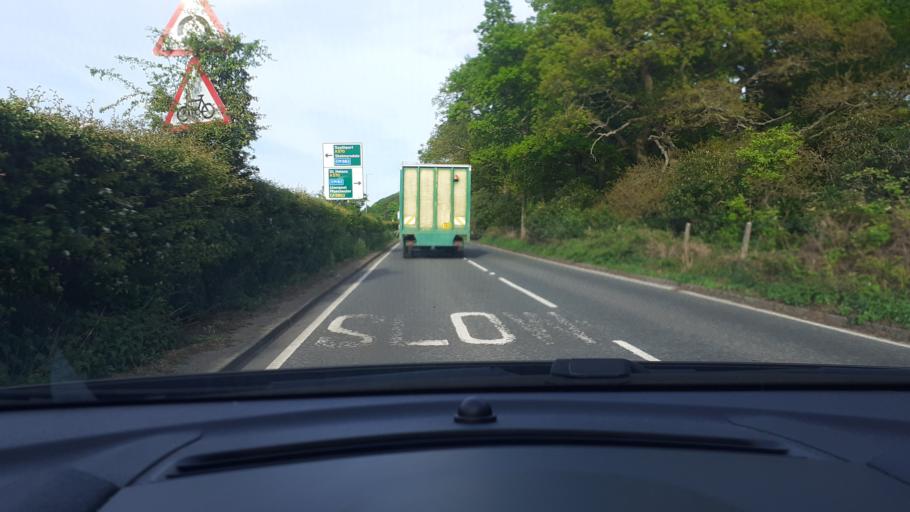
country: GB
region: England
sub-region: St. Helens
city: Rainford
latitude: 53.5159
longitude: -2.8085
